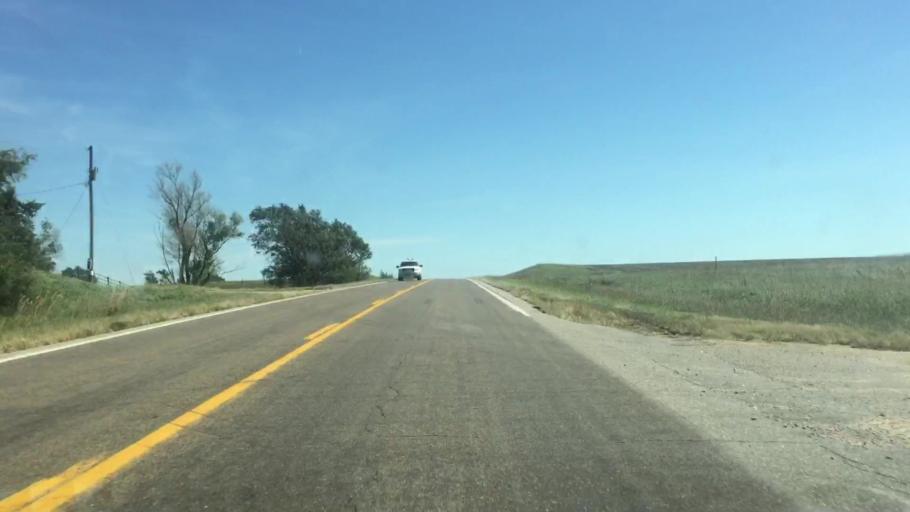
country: US
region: Nebraska
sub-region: Thayer County
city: Hebron
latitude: 40.1472
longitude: -97.5386
